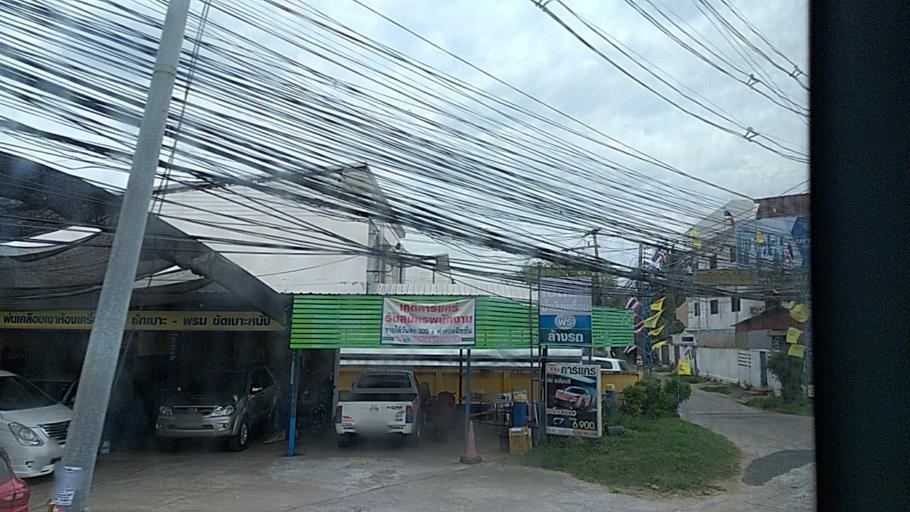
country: TH
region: Maha Sarakham
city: Maha Sarakham
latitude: 16.1766
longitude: 103.3140
